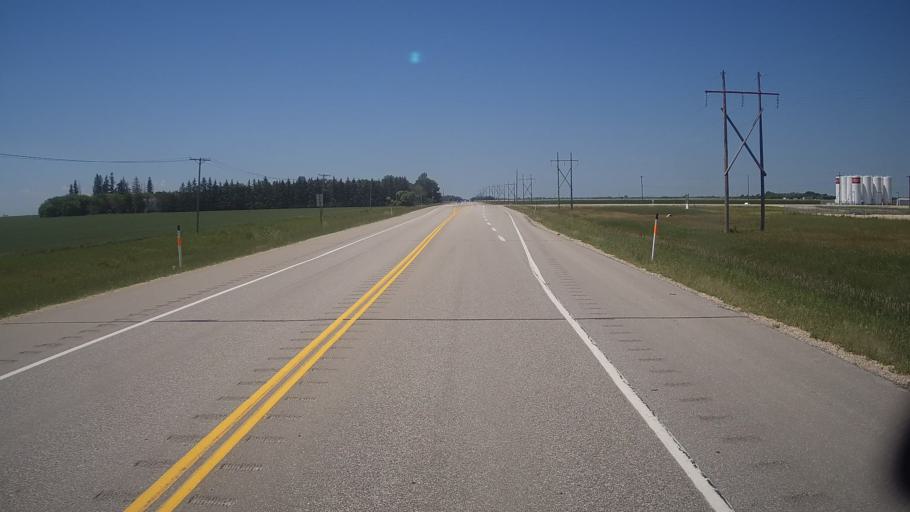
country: CA
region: Manitoba
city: Stonewall
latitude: 50.1231
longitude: -97.5406
